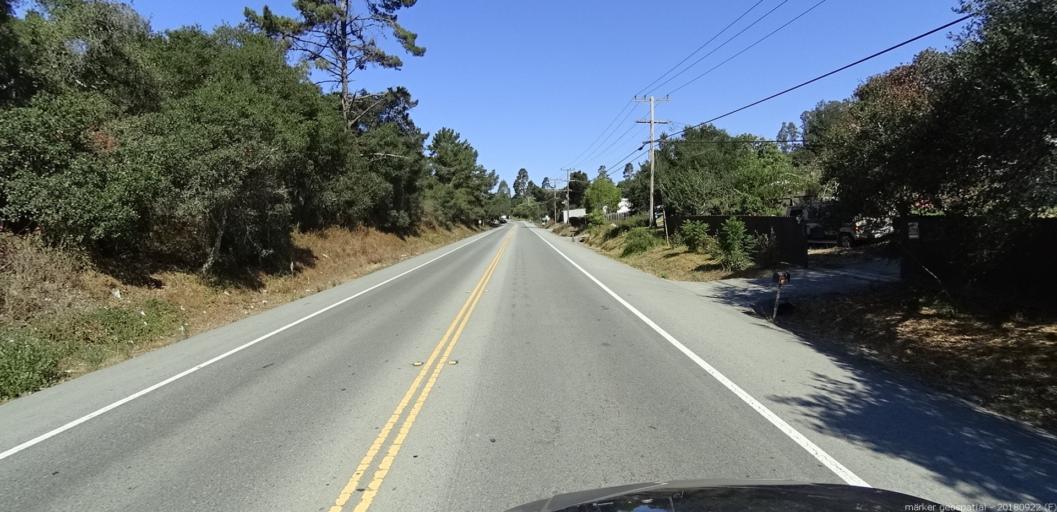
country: US
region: California
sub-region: Monterey County
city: Prunedale
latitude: 36.8268
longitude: -121.6767
